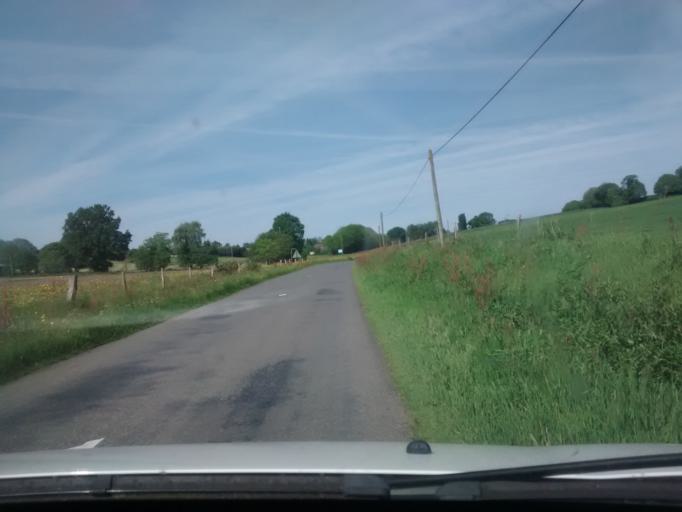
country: FR
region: Brittany
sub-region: Departement d'Ille-et-Vilaine
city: Javene
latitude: 48.3364
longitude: -1.2395
